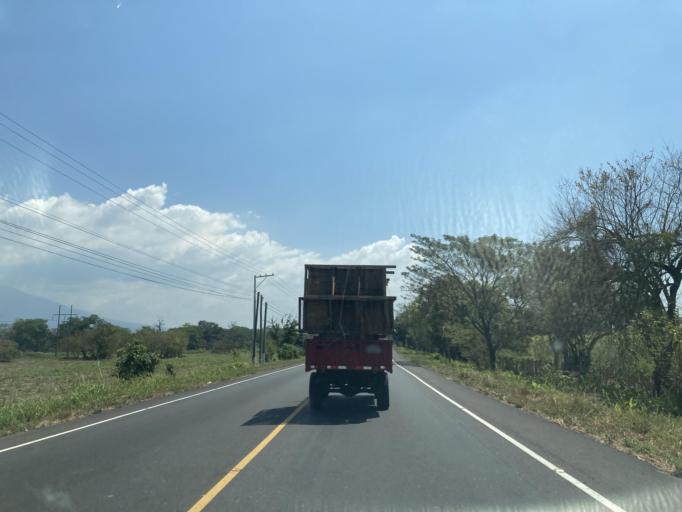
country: GT
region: Escuintla
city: Guanagazapa
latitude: 14.1002
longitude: -90.6116
